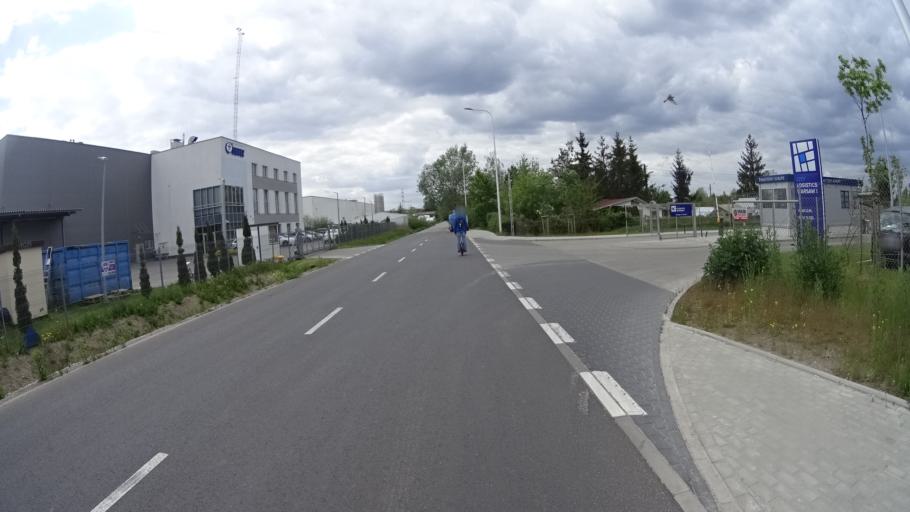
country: PL
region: Masovian Voivodeship
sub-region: Powiat warszawski zachodni
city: Babice
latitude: 52.2775
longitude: 20.8704
